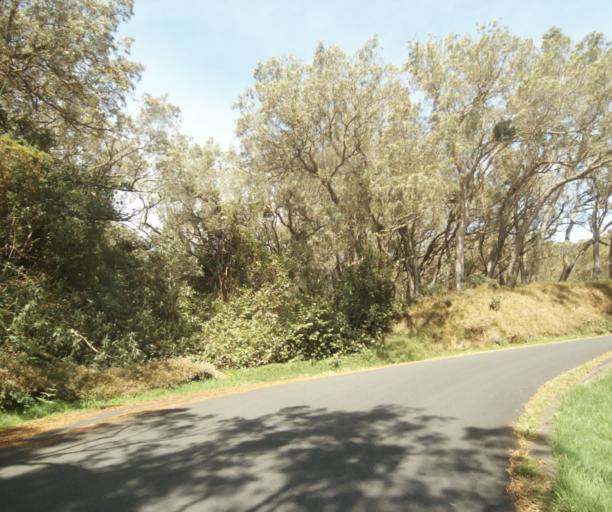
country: RE
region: Reunion
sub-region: Reunion
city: Trois-Bassins
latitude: -21.0590
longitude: 55.3662
